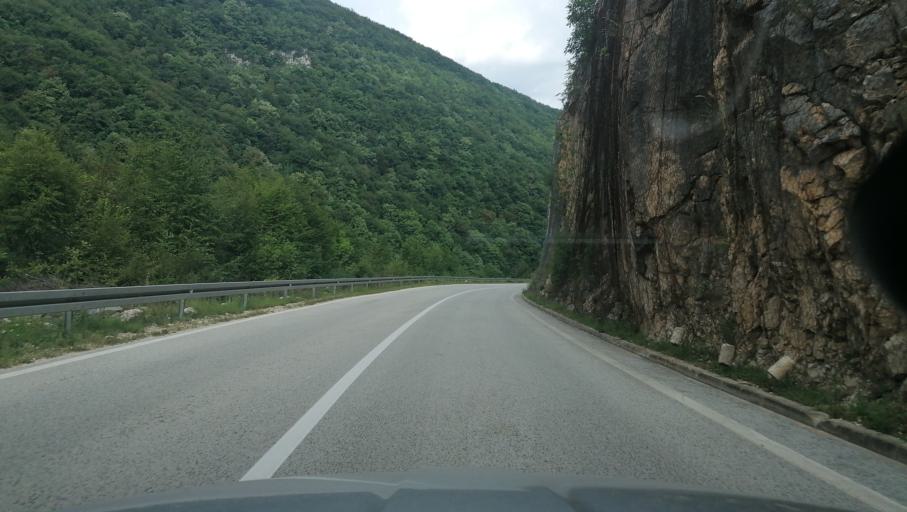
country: BA
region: Republika Srpska
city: Mrkonjic Grad
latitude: 44.4614
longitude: 17.1864
